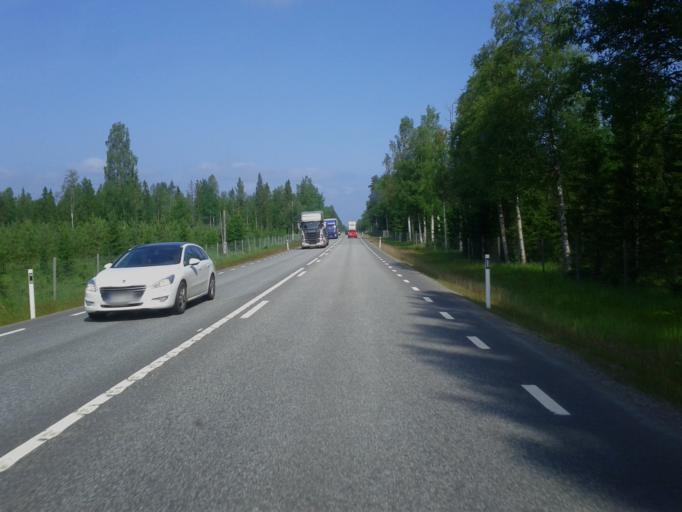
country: SE
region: Vaesterbotten
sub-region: Skelleftea Kommun
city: Burea
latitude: 64.5695
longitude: 21.2263
